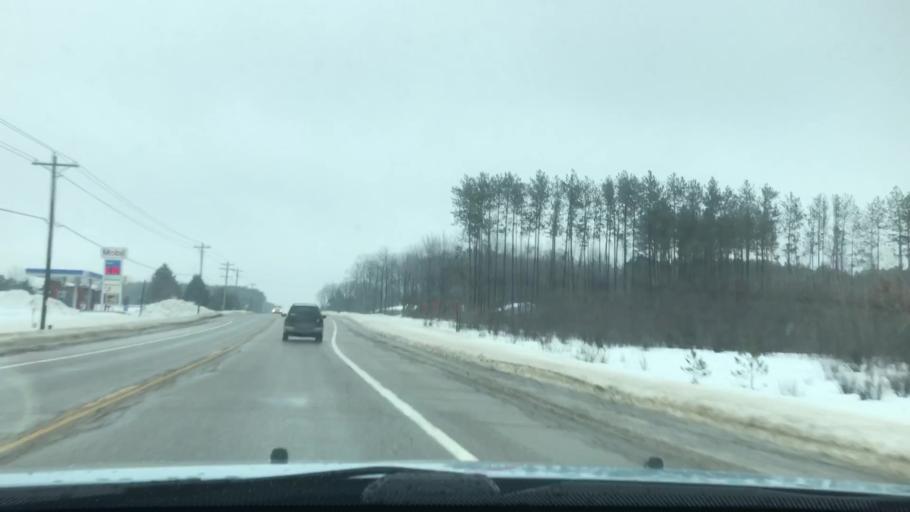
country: US
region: Michigan
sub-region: Otsego County
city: Gaylord
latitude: 45.0276
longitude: -84.7416
